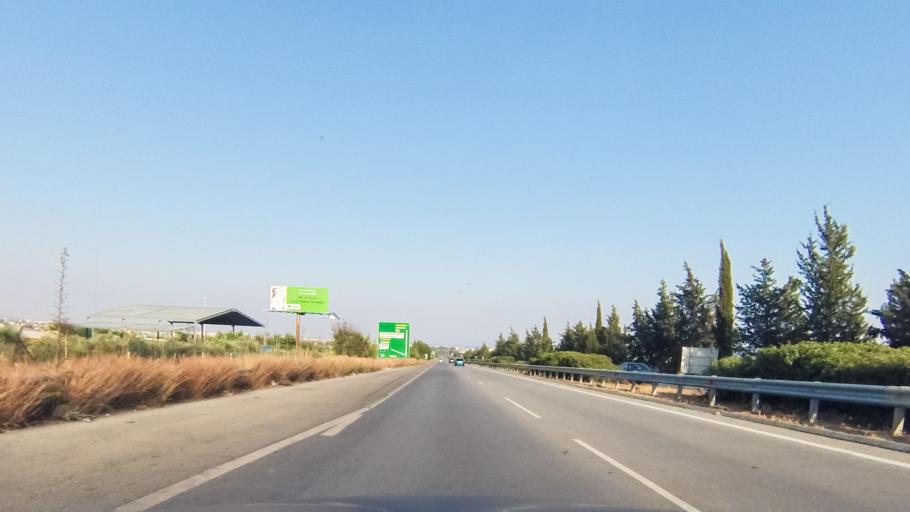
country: CY
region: Limassol
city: Ypsonas
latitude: 34.6934
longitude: 32.9720
